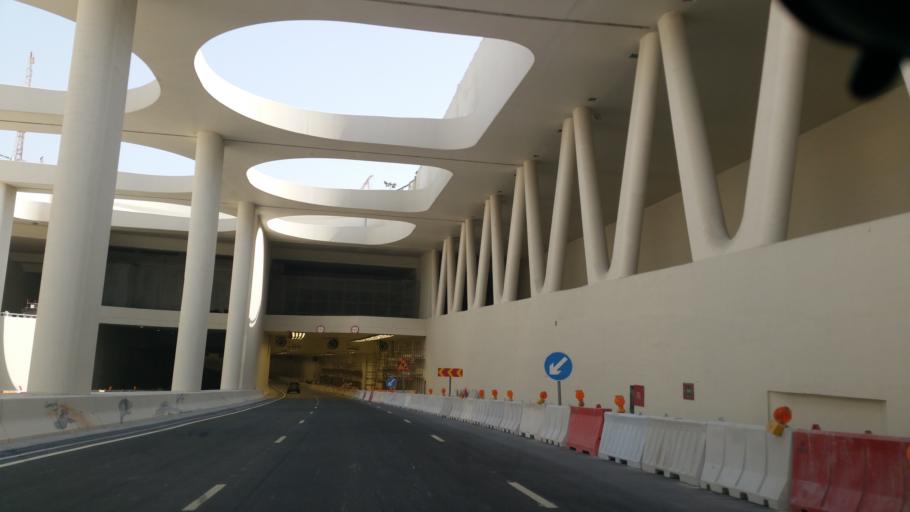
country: QA
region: Baladiyat Umm Salal
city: Umm Salal Muhammad
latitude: 25.4205
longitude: 51.5060
